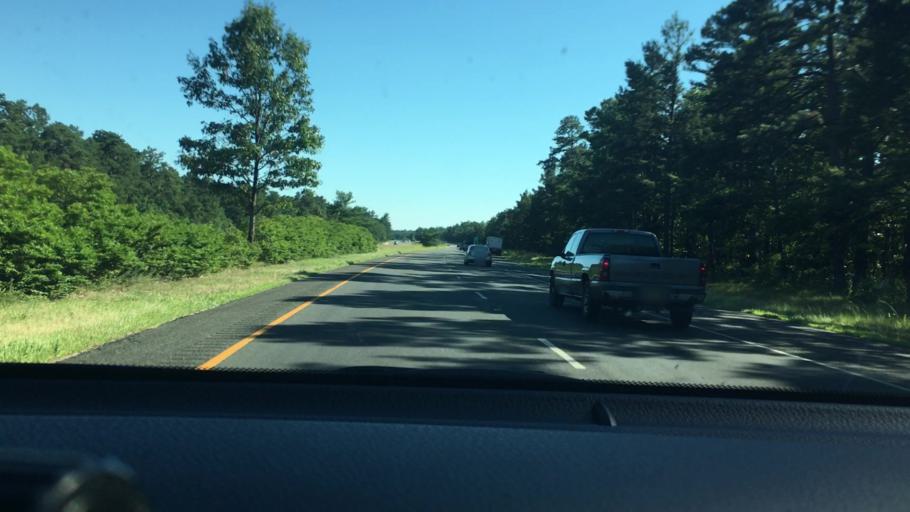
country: US
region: New Jersey
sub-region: Gloucester County
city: Newfield
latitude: 39.5322
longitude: -75.0646
